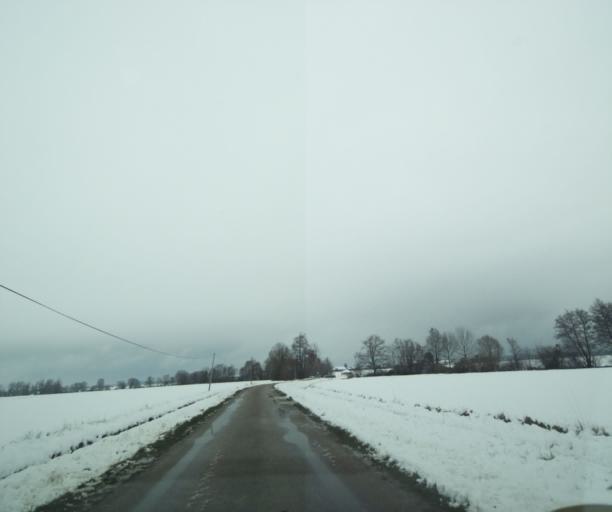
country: FR
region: Champagne-Ardenne
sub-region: Departement de la Haute-Marne
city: Montier-en-Der
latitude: 48.4334
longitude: 4.7937
